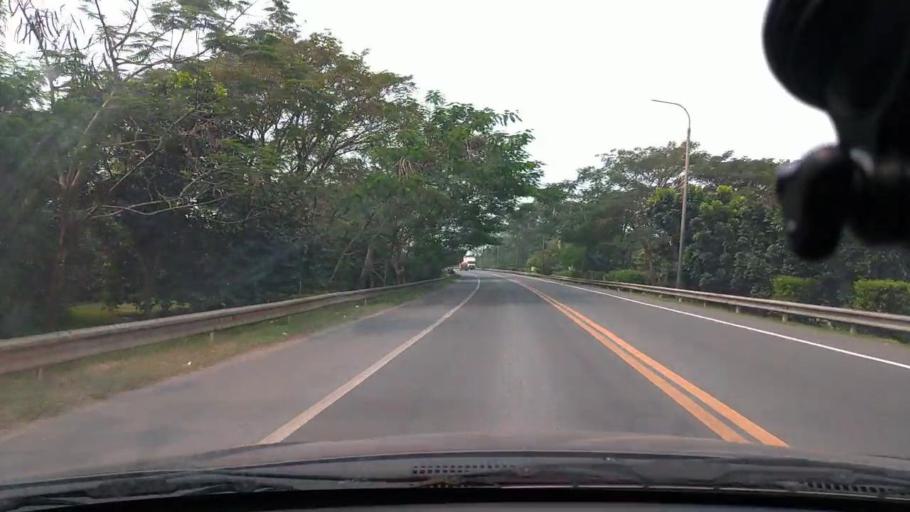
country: ID
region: Banten
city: Serang
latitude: -6.0910
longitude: 106.1387
